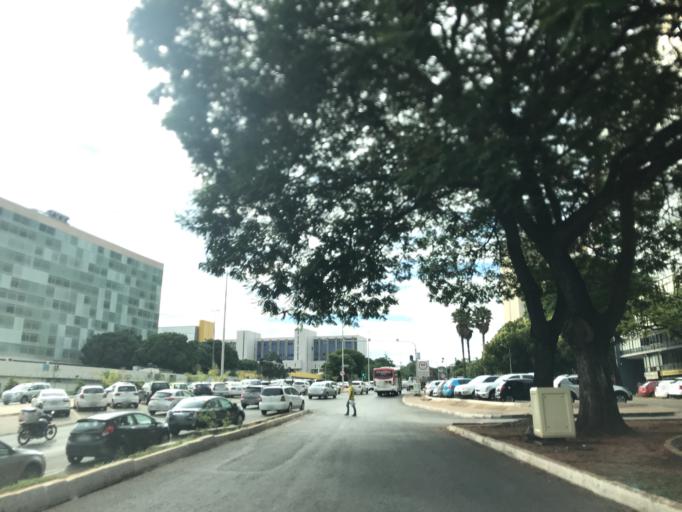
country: BR
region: Federal District
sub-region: Brasilia
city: Brasilia
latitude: -15.8001
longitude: -47.8864
